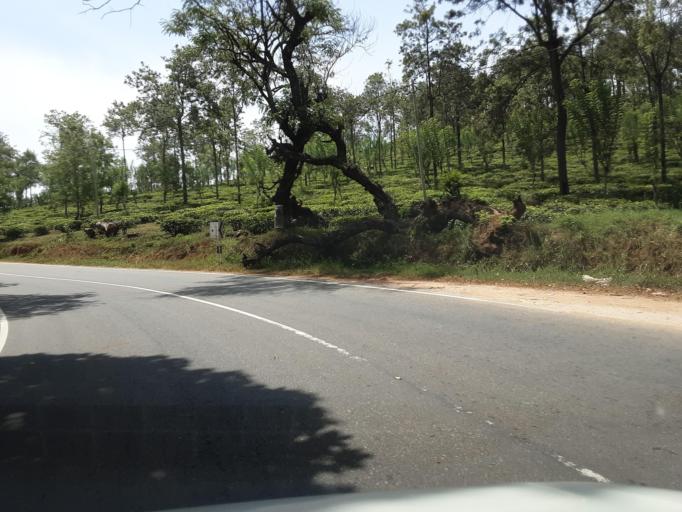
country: LK
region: Central
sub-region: Nuwara Eliya District
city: Nuwara Eliya
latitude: 6.9441
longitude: 80.9142
